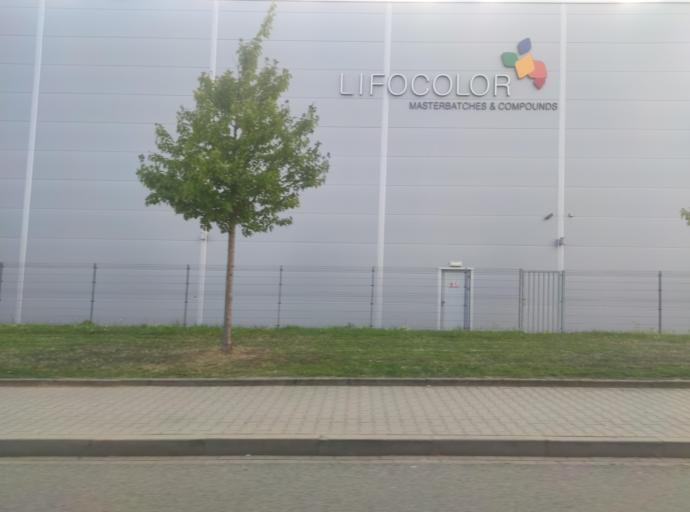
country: CZ
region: South Moravian
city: Podoli
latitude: 49.1749
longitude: 16.6697
